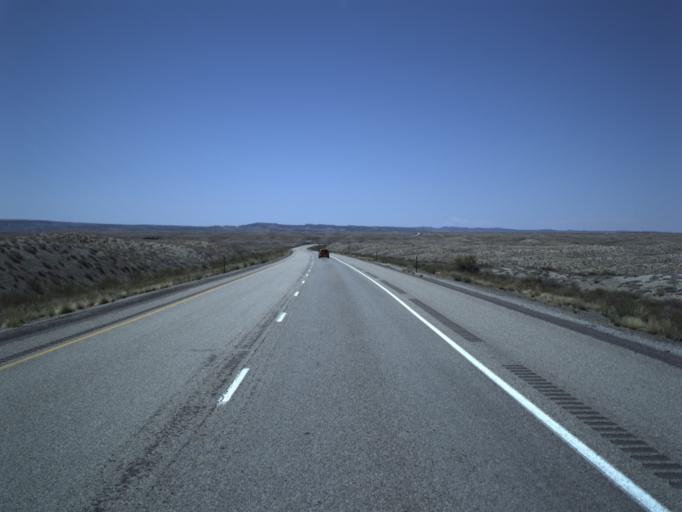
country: US
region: Utah
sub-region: Grand County
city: Moab
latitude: 38.9913
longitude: -109.3341
